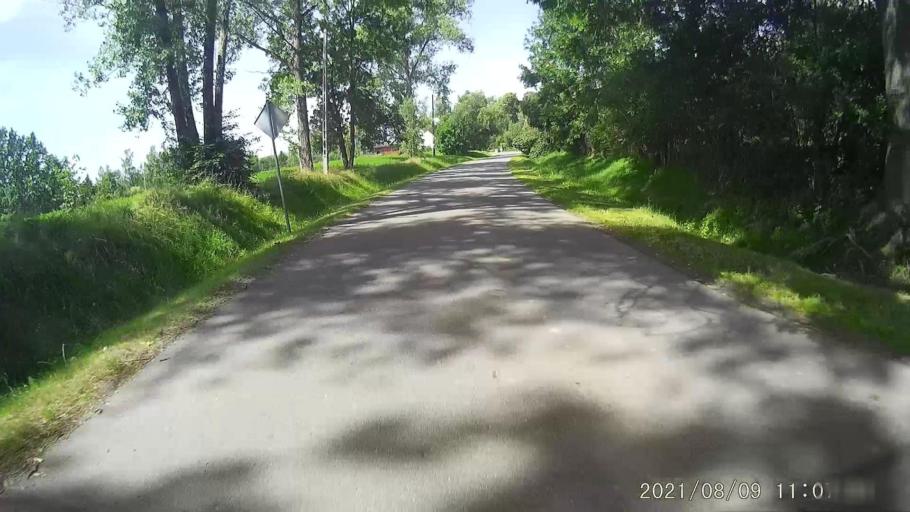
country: PL
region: Lower Silesian Voivodeship
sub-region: Powiat klodzki
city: Klodzko
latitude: 50.4555
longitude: 16.6034
